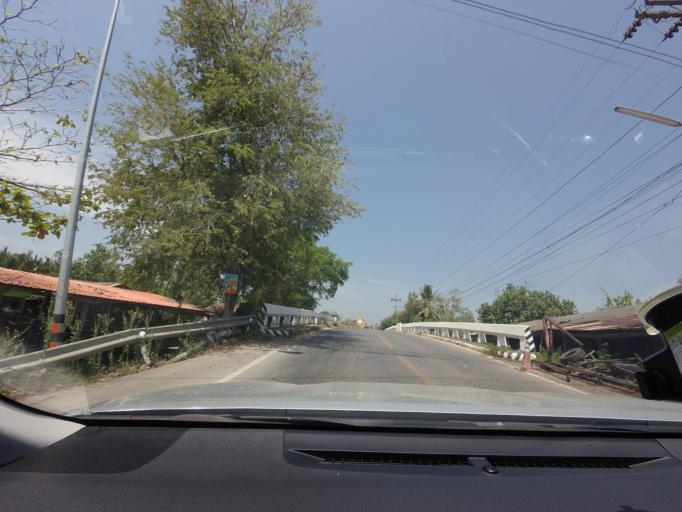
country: TH
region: Surat Thani
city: Tha Chang
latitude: 9.2024
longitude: 99.2436
